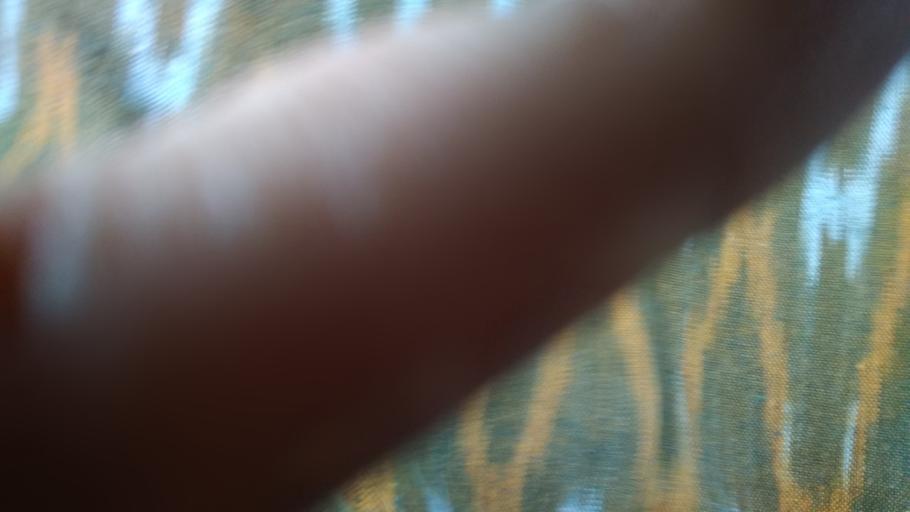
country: IN
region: Telangana
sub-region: Hyderabad
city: Malkajgiri
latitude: 17.4365
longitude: 78.5550
